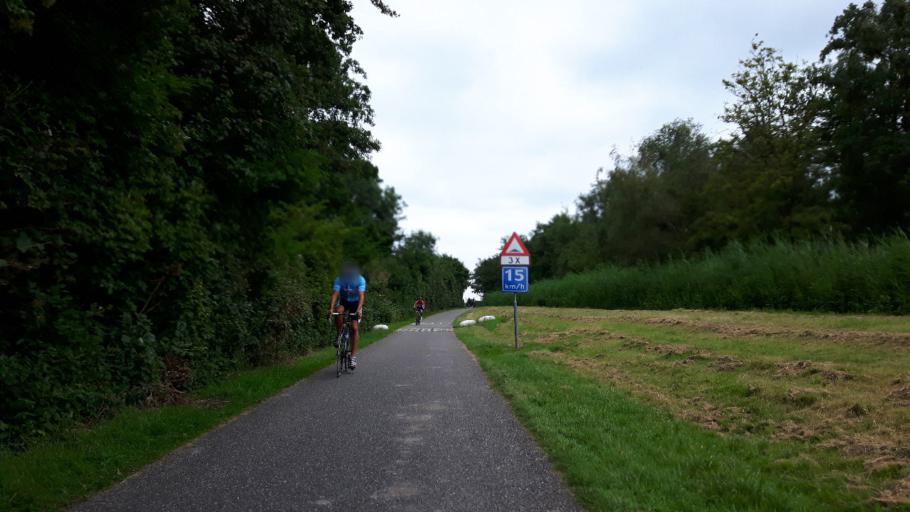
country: NL
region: South Holland
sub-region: Gemeente Lansingerland
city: Bleiswijk
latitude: 52.0087
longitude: 4.5601
